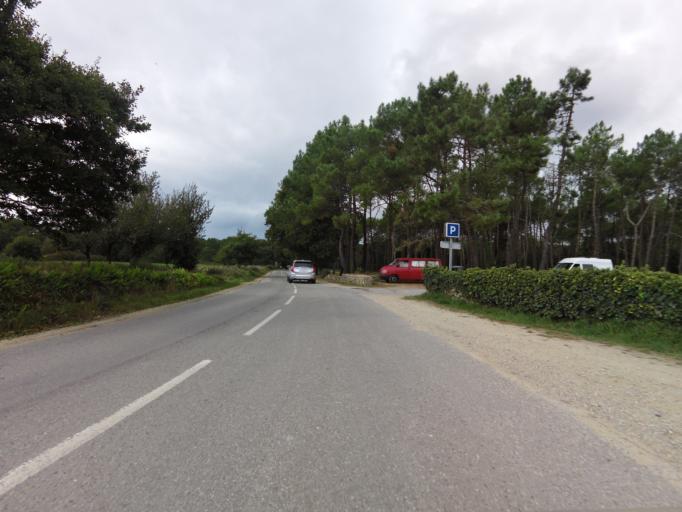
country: FR
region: Brittany
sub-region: Departement du Morbihan
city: Carnac
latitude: 47.5963
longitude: -3.0681
